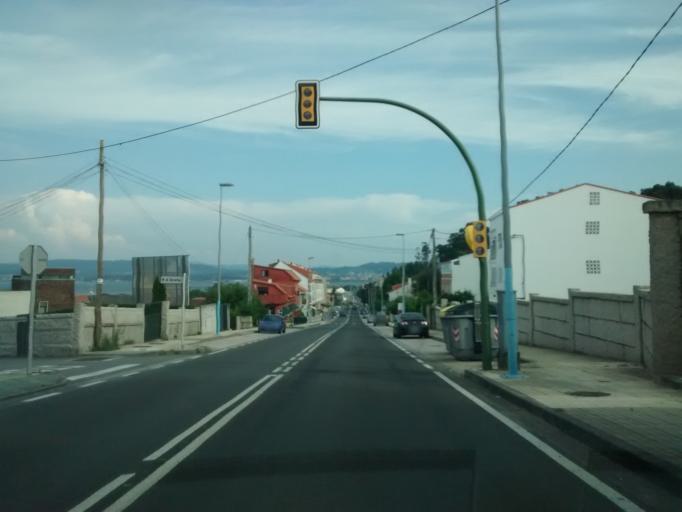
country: ES
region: Galicia
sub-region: Provincia de Pontevedra
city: O Grove
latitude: 42.4853
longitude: -8.8651
